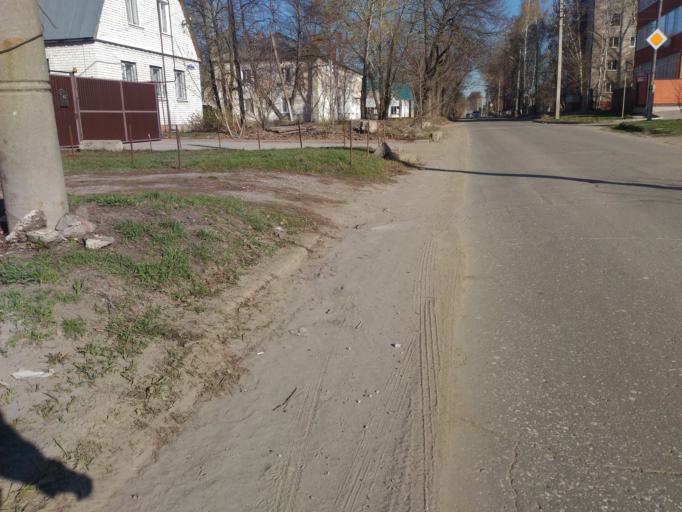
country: RU
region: Ulyanovsk
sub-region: Ulyanovskiy Rayon
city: Ulyanovsk
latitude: 54.3452
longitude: 48.3819
